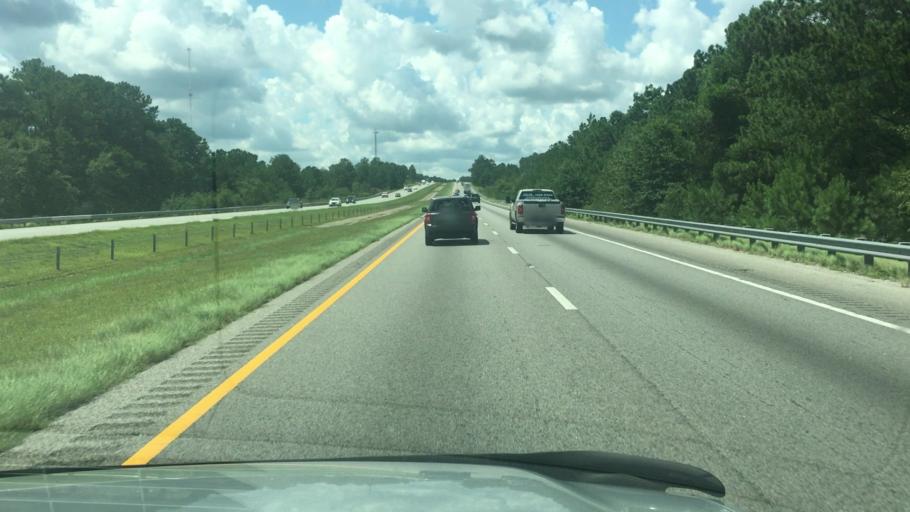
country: US
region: South Carolina
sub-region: Kershaw County
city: Lugoff
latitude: 34.1780
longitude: -80.7036
